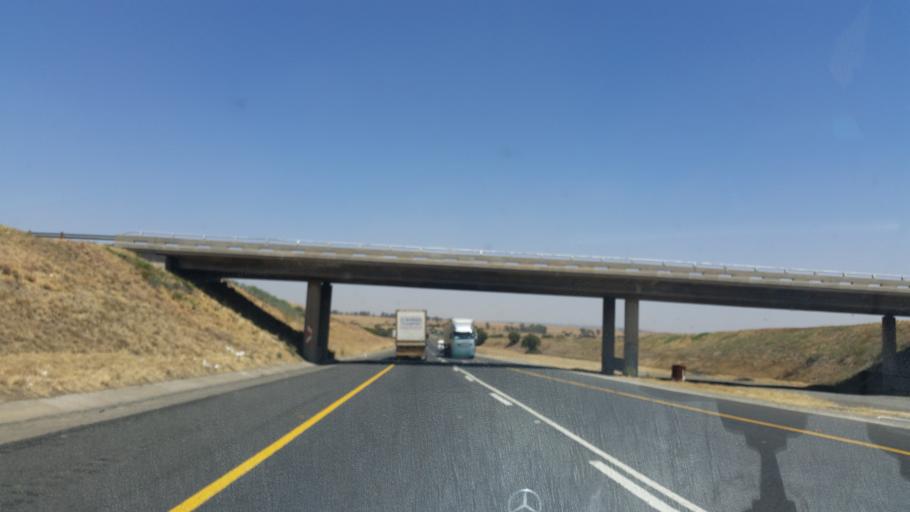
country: ZA
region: Orange Free State
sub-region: Lejweleputswa District Municipality
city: Winburg
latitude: -28.6270
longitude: 26.9106
